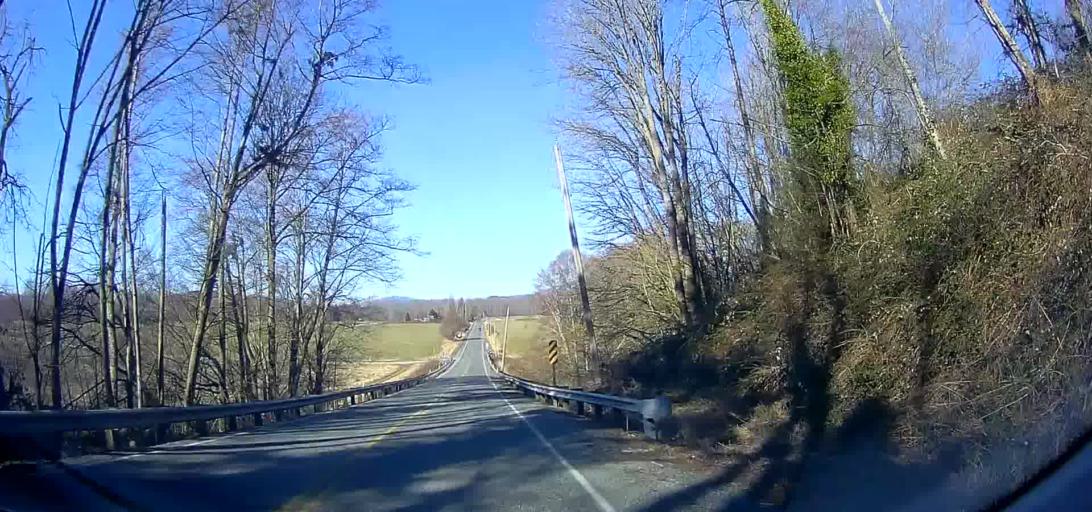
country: US
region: Washington
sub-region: Skagit County
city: Burlington
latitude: 48.4561
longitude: -122.3028
